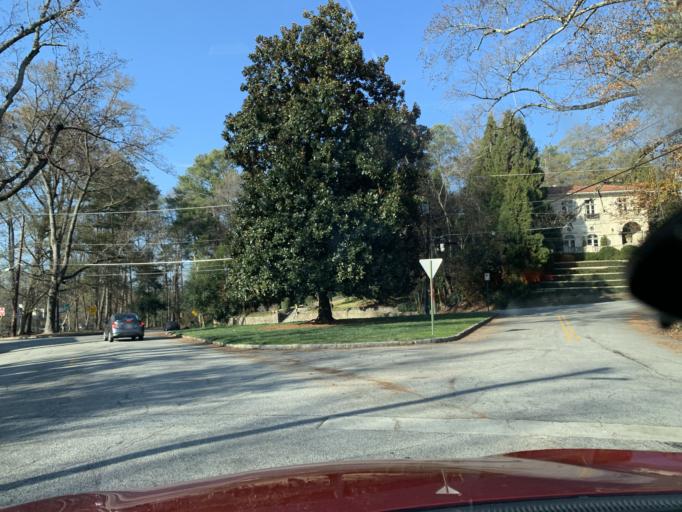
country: US
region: Georgia
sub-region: DeKalb County
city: Druid Hills
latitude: 33.7967
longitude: -84.3745
